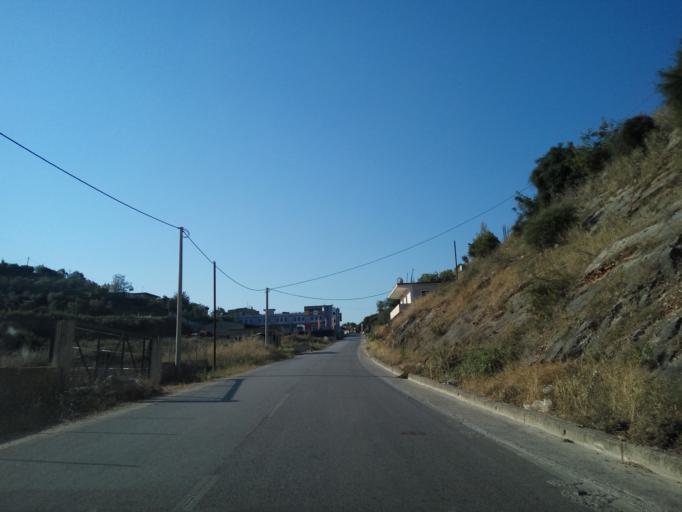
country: AL
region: Vlore
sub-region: Rrethi i Sarandes
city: Sarande
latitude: 39.8798
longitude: 20.0231
